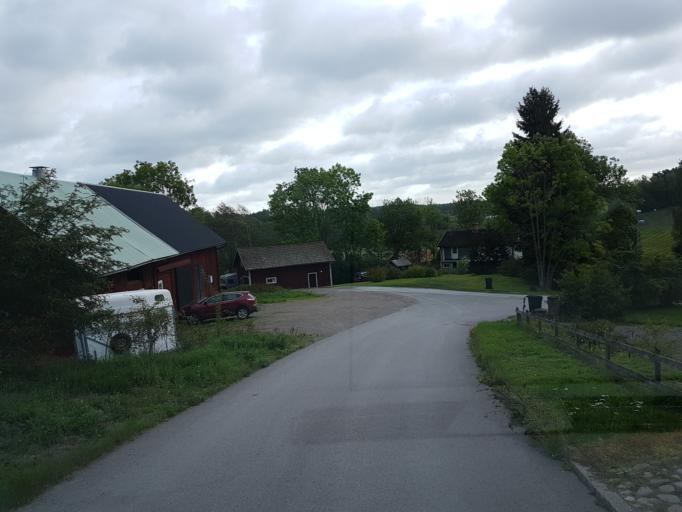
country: SE
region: OEstergoetland
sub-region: Atvidabergs Kommun
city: Atvidaberg
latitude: 58.2185
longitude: 16.0299
